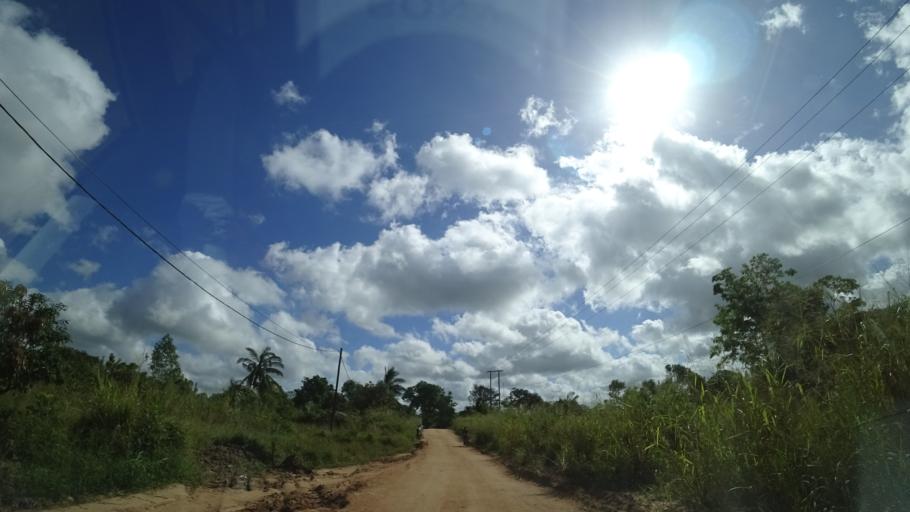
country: MZ
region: Sofala
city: Dondo
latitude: -19.3907
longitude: 34.7084
